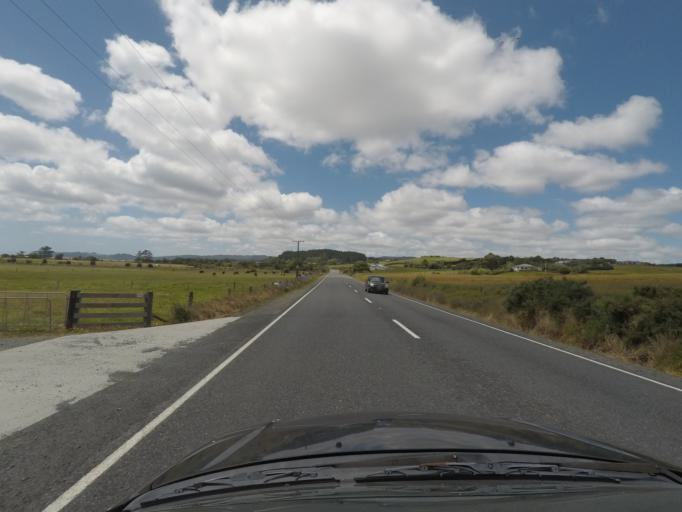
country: NZ
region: Northland
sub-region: Whangarei
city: Ruakaka
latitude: -36.0101
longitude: 174.4813
